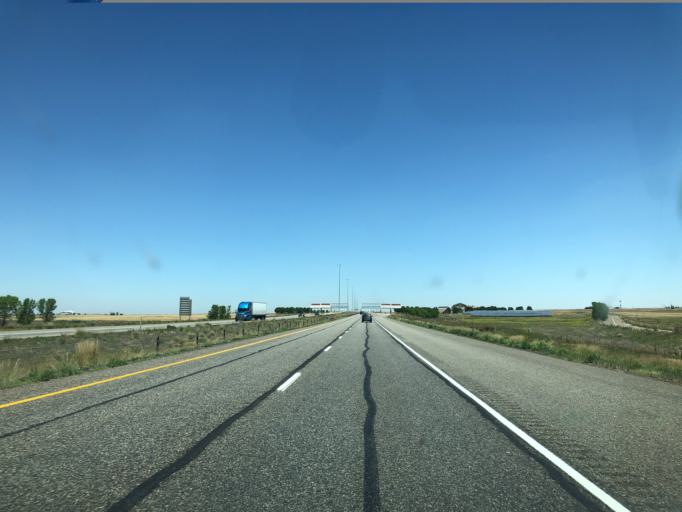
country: US
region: Colorado
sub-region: Adams County
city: Aurora
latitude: 39.7649
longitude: -104.7164
